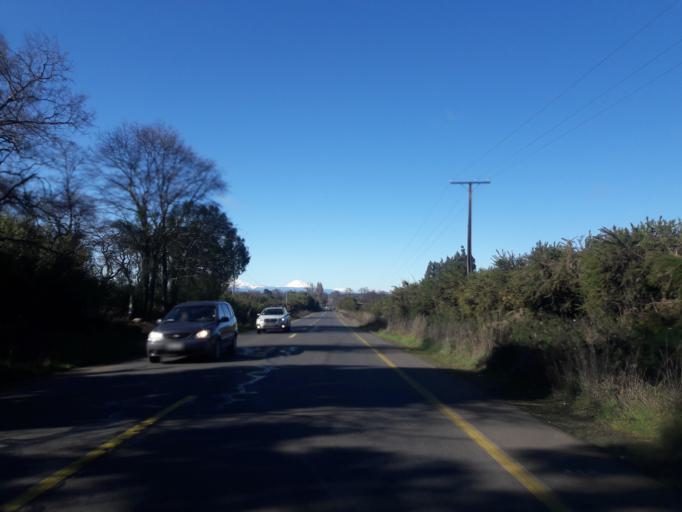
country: CL
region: Araucania
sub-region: Provincia de Malleco
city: Victoria
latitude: -38.2568
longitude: -72.2674
